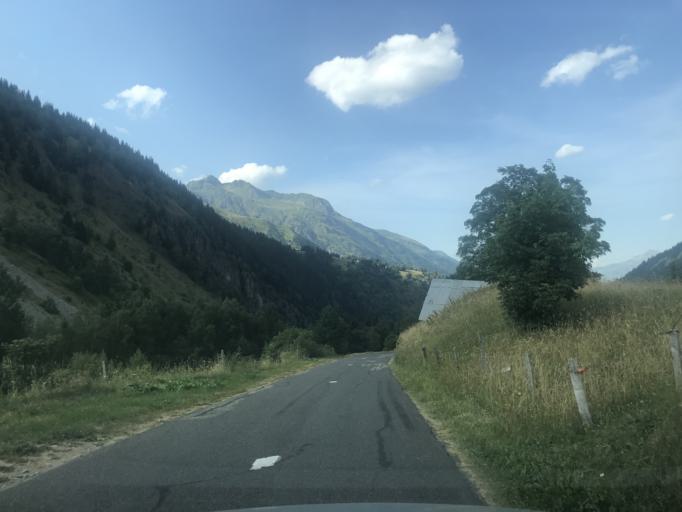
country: FR
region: Rhone-Alpes
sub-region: Departement de la Savoie
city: Saint-Etienne-de-Cuines
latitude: 45.2633
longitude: 6.1961
